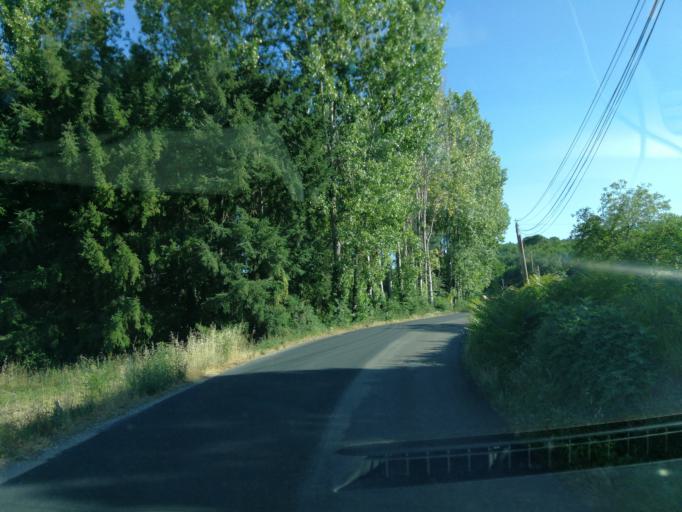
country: FR
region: Midi-Pyrenees
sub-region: Departement du Lot
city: Gourdon
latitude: 44.7659
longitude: 1.3709
